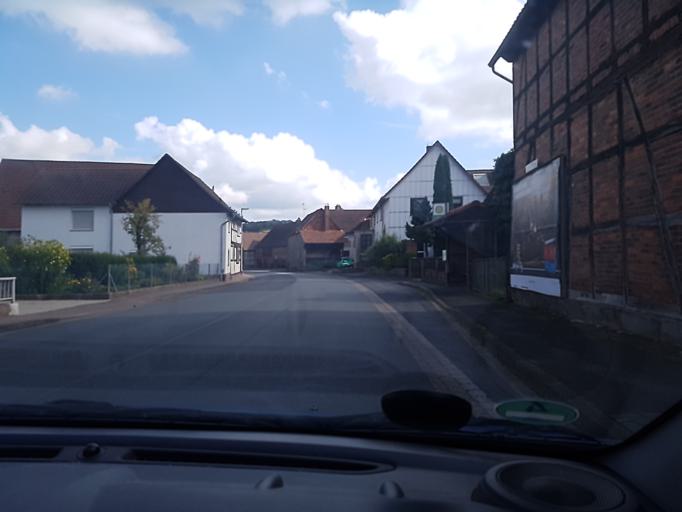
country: DE
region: Lower Saxony
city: Uslar
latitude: 51.6699
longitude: 9.5979
